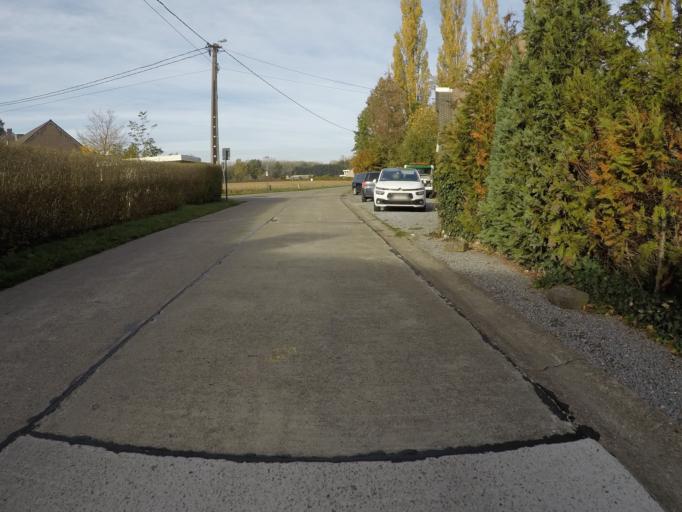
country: BE
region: Flanders
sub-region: Provincie Vlaams-Brabant
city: Begijnendijk
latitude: 51.0082
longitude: 4.7698
